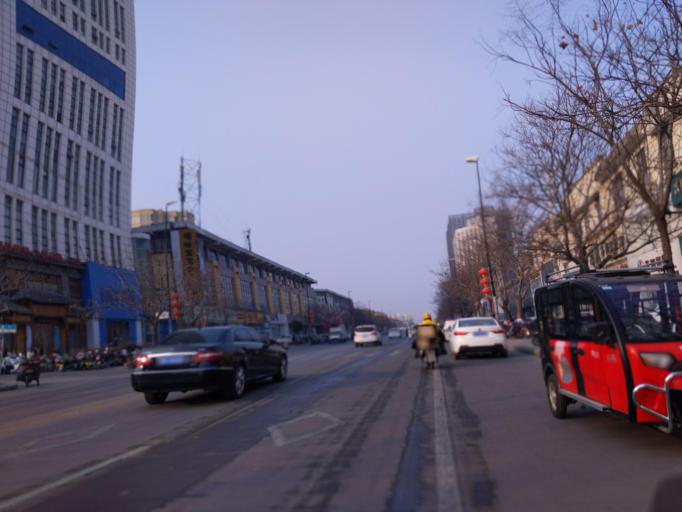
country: CN
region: Henan Sheng
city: Zhongyuanlu
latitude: 35.7677
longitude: 115.0581
